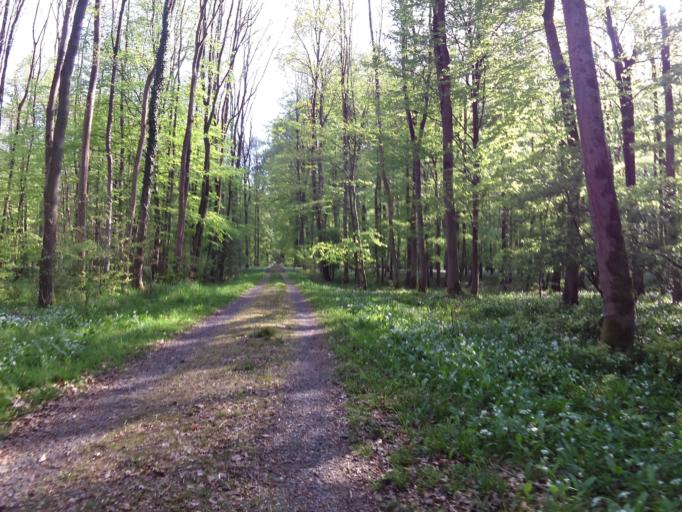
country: DE
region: Hesse
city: Morfelden-Walldorf
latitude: 49.9790
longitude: 8.5262
